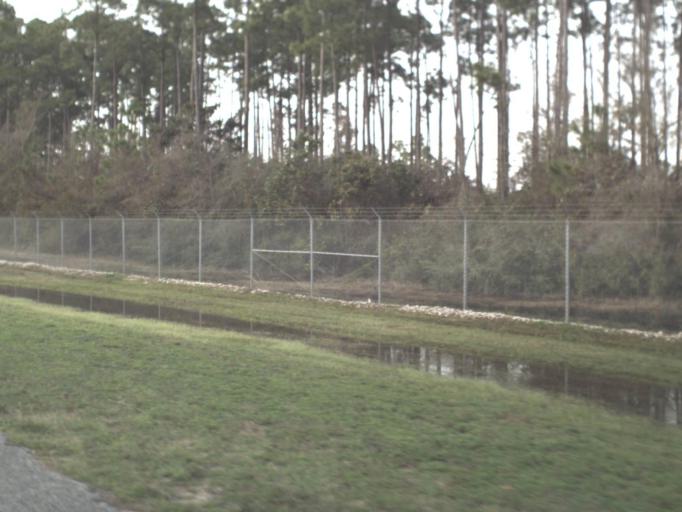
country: US
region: Florida
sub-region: Bay County
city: Tyndall Air Force Base
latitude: 30.0584
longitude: -85.5752
